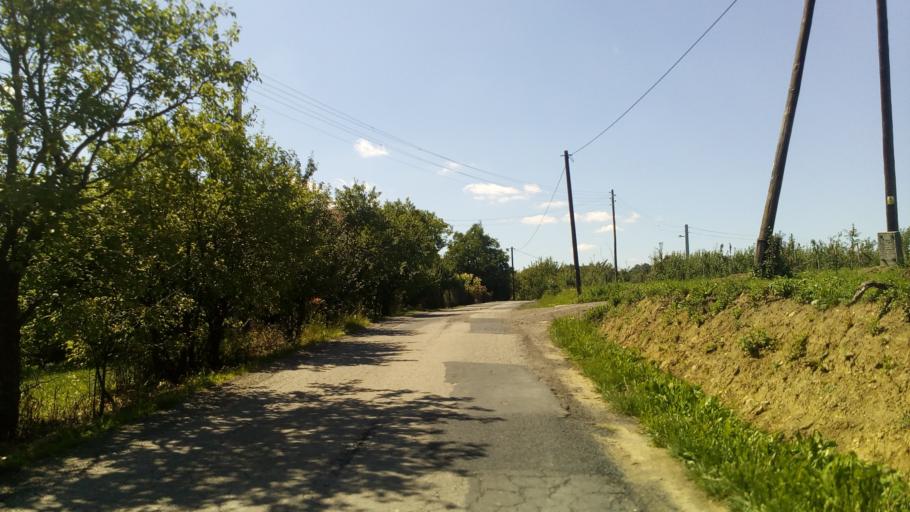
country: PL
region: Lesser Poland Voivodeship
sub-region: Powiat nowosadecki
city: Olszana
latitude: 49.5617
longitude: 20.5007
